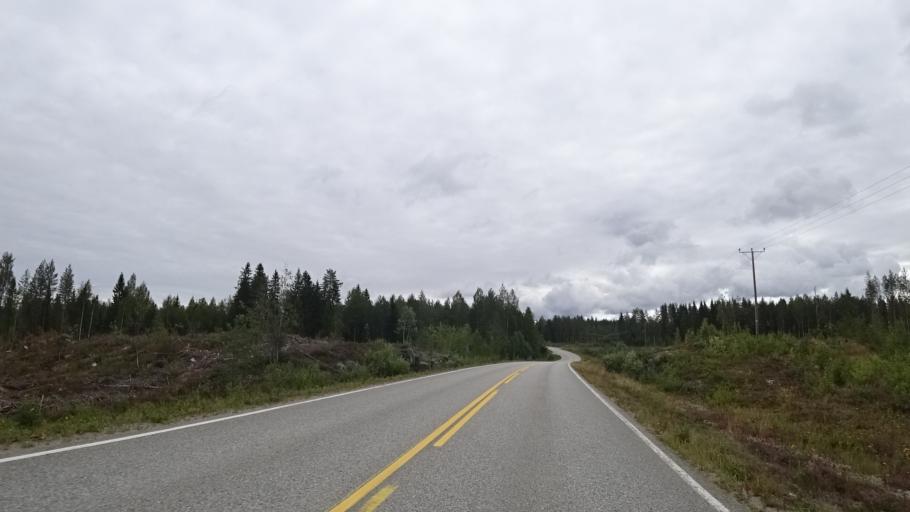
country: FI
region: North Karelia
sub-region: Joensuu
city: Ilomantsi
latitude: 62.6245
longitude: 31.2459
